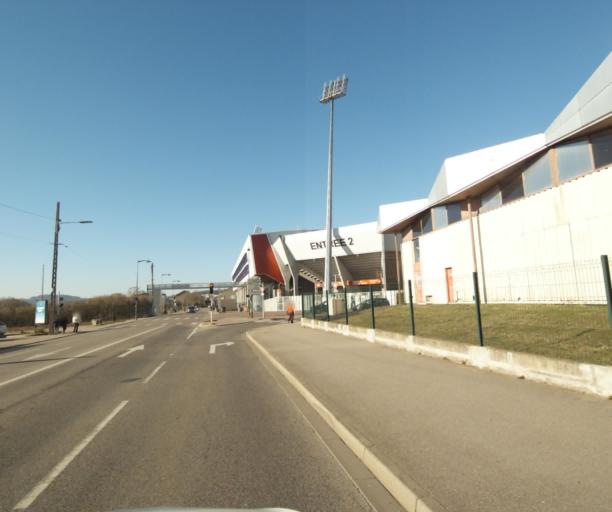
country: FR
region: Lorraine
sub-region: Departement de Meurthe-et-Moselle
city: Saint-Max
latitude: 48.6940
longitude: 6.2109
